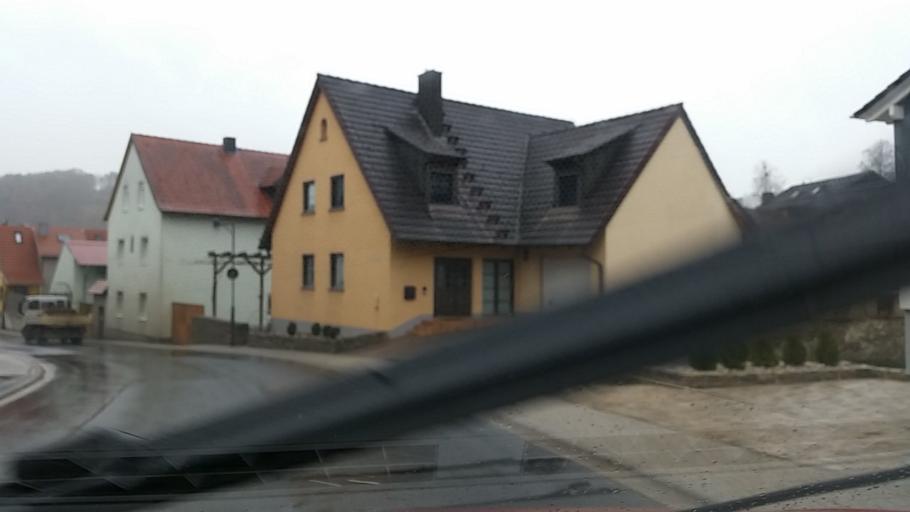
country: DE
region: Bavaria
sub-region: Regierungsbezirk Unterfranken
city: Retzstadt
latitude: 49.9137
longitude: 9.8825
